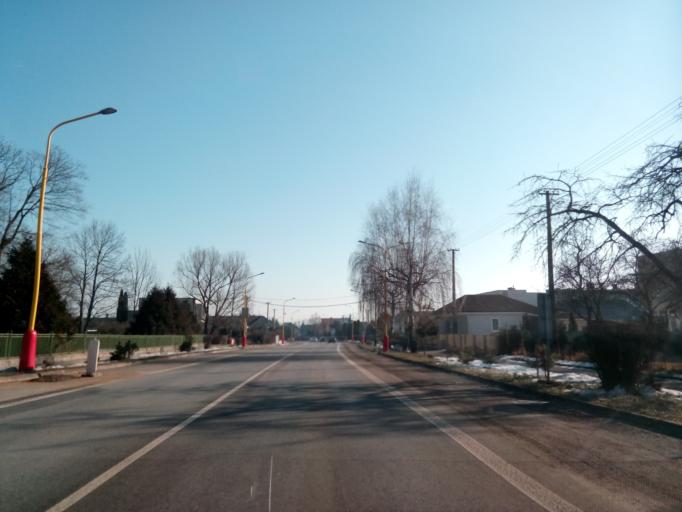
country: SK
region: Kosicky
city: Secovce
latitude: 48.7020
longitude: 21.6682
